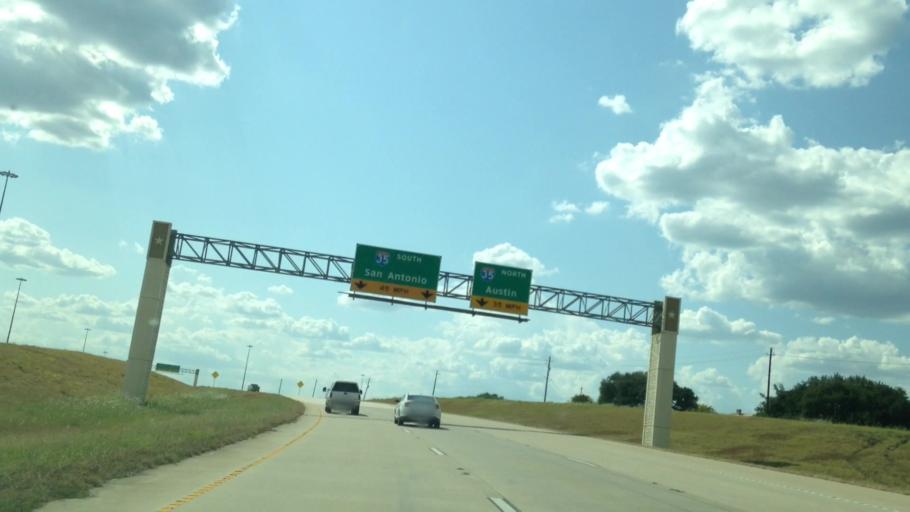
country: US
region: Texas
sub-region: Travis County
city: Onion Creek
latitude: 30.1119
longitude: -97.7975
